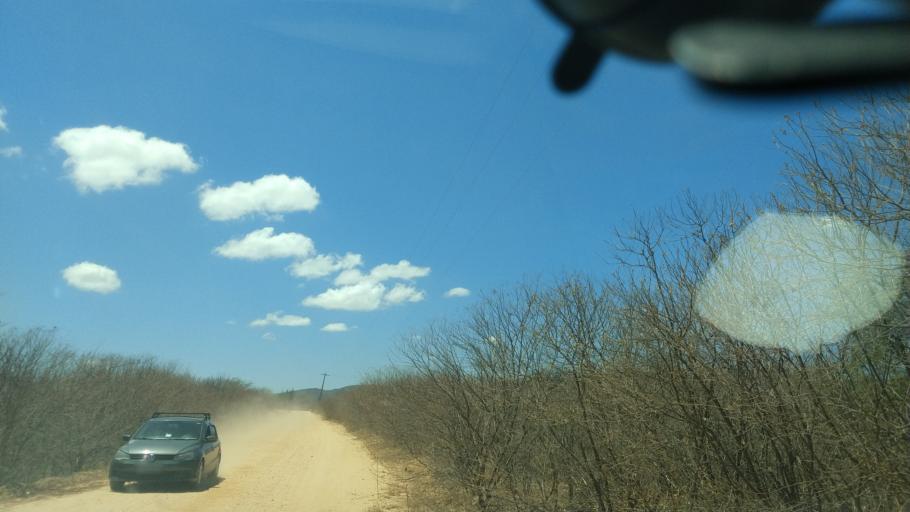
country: BR
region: Rio Grande do Norte
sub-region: Cerro Cora
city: Cerro Cora
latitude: -6.0116
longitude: -36.2948
